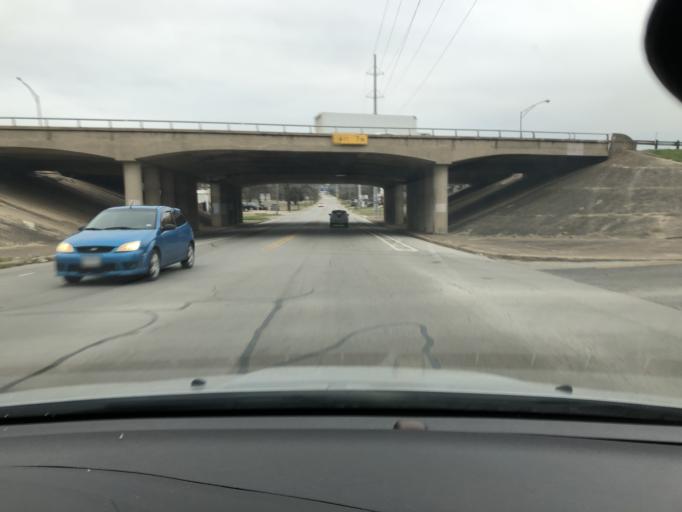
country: US
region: Texas
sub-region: Tarrant County
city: Fort Worth
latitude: 32.7267
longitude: -97.2987
